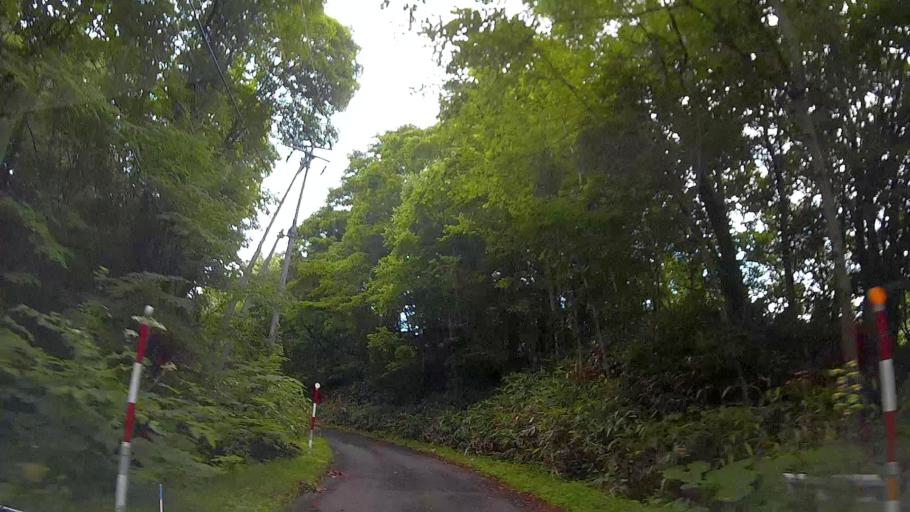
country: JP
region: Hokkaido
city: Nanae
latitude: 42.1046
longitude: 140.4523
